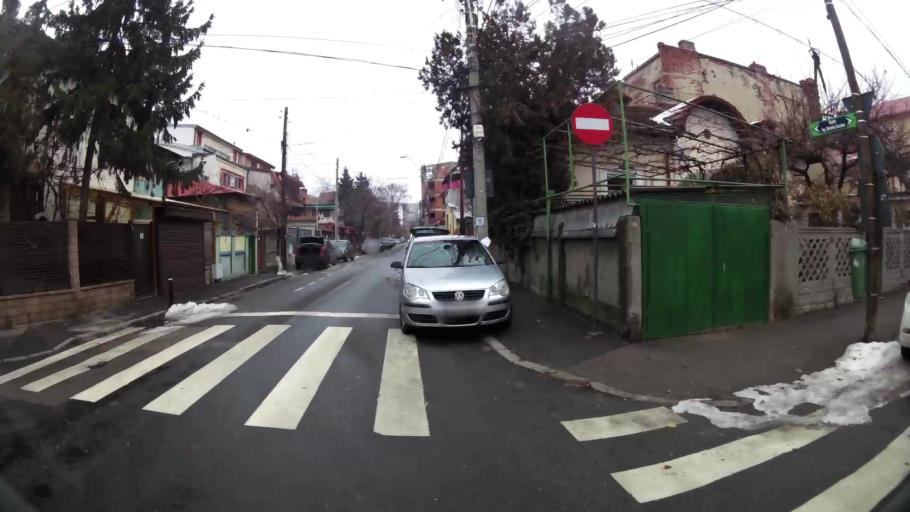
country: RO
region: Bucuresti
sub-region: Municipiul Bucuresti
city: Bucuresti
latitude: 44.4623
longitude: 26.0658
